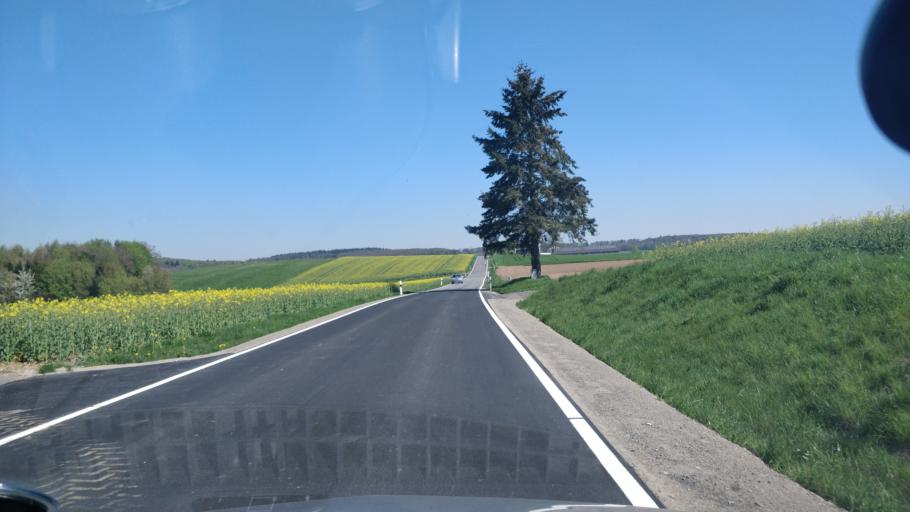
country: DE
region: Hesse
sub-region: Regierungsbezirk Giessen
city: Dehrn
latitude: 50.4616
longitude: 8.0979
